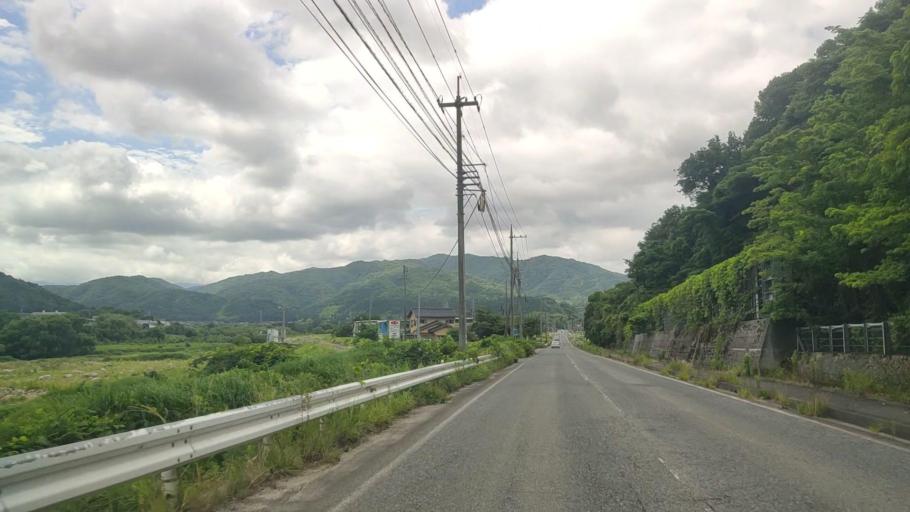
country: JP
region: Tottori
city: Yonago
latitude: 35.3364
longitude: 133.4342
